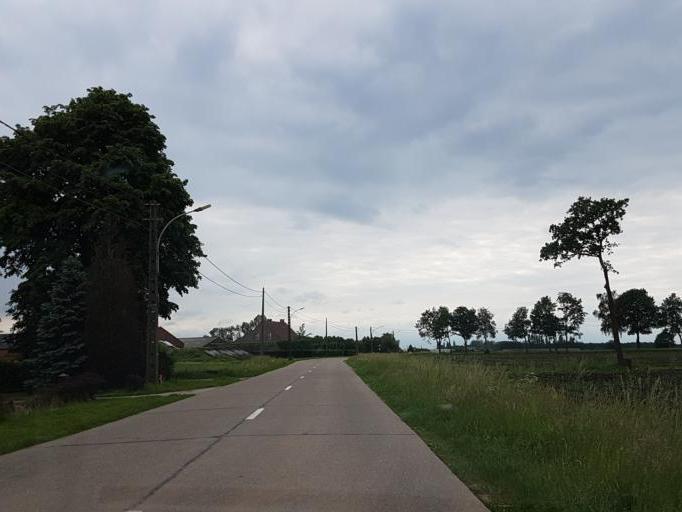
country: BE
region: Flanders
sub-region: Provincie Antwerpen
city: Rijkevorsel
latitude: 51.3638
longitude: 4.7944
